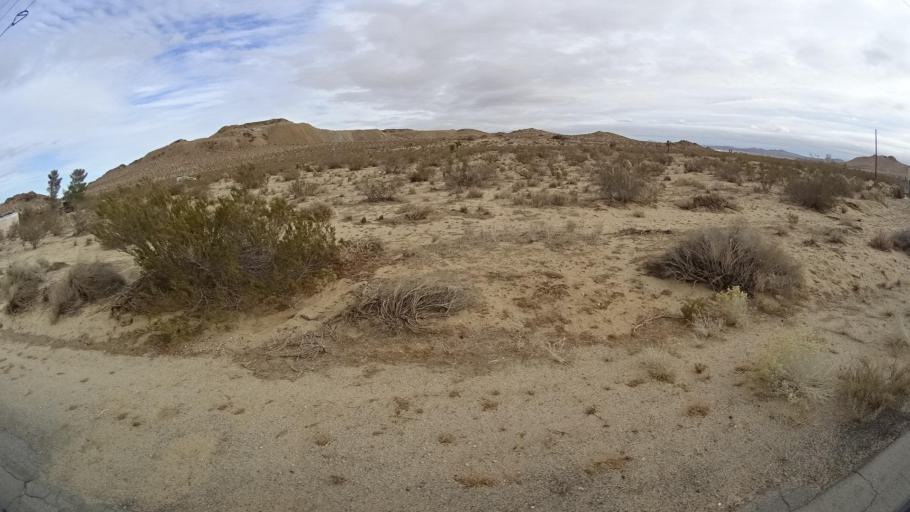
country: US
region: California
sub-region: Kern County
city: Mojave
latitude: 35.0022
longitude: -118.1866
